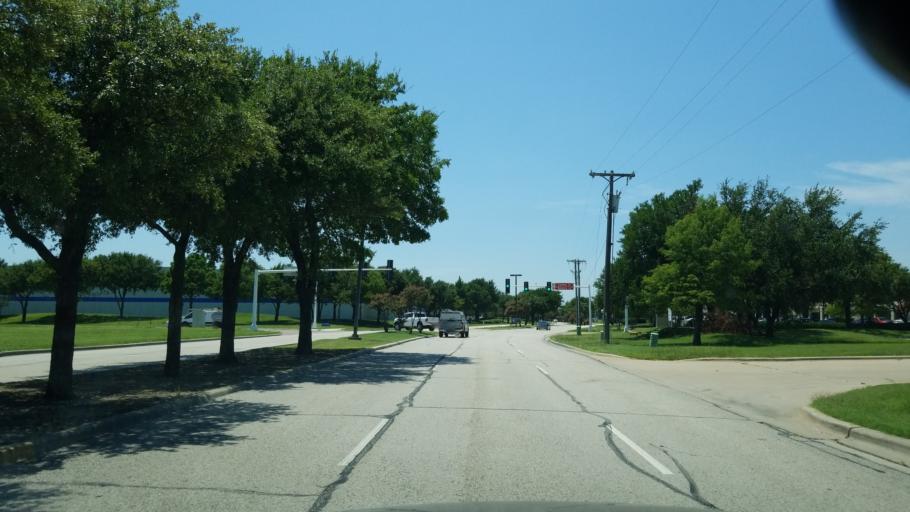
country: US
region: Texas
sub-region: Dallas County
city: Farmers Branch
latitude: 32.9386
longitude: -96.9052
